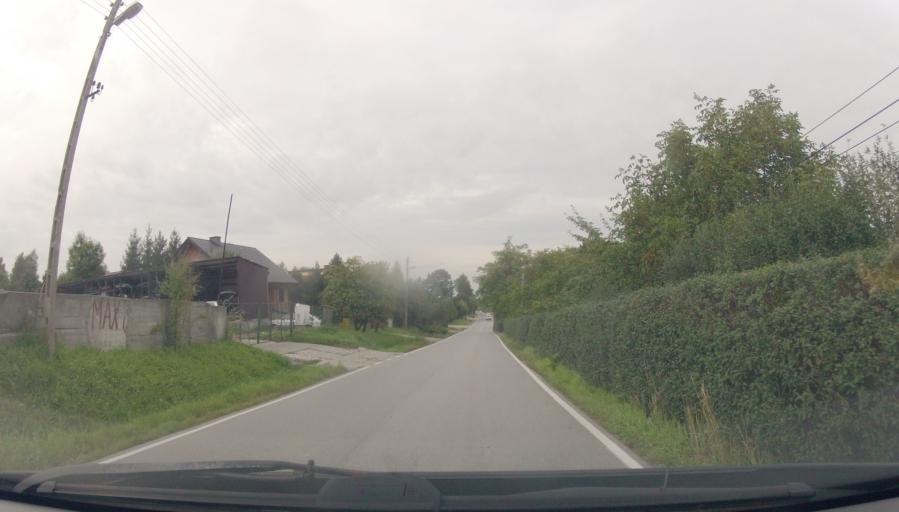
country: PL
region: Lesser Poland Voivodeship
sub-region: Powiat wielicki
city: Pawlikowice
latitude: 49.9761
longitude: 20.0289
